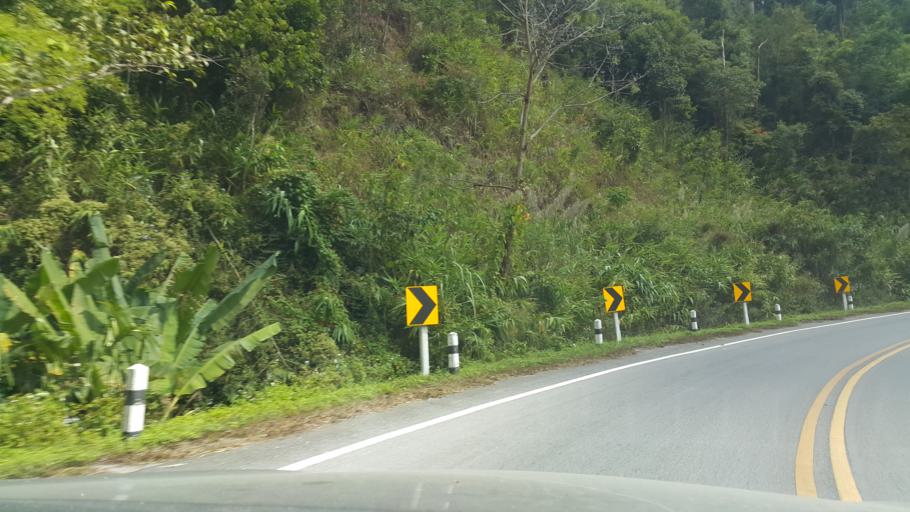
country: TH
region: Phayao
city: Phayao
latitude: 19.0729
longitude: 99.7724
